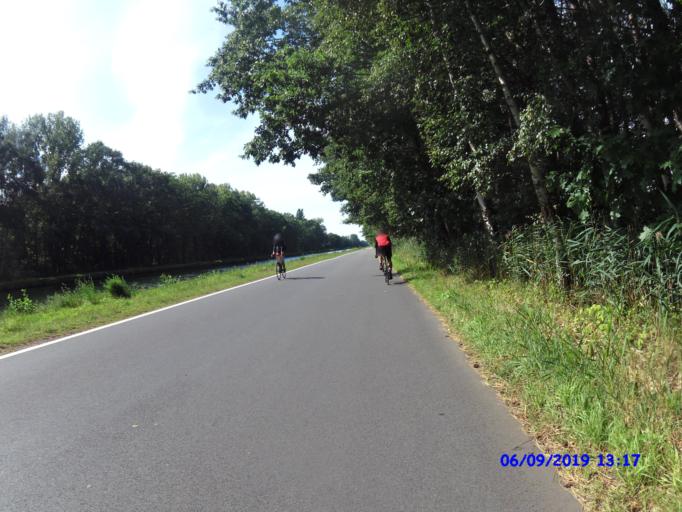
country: BE
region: Flanders
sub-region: Provincie Antwerpen
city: Geel
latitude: 51.2109
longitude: 5.0338
